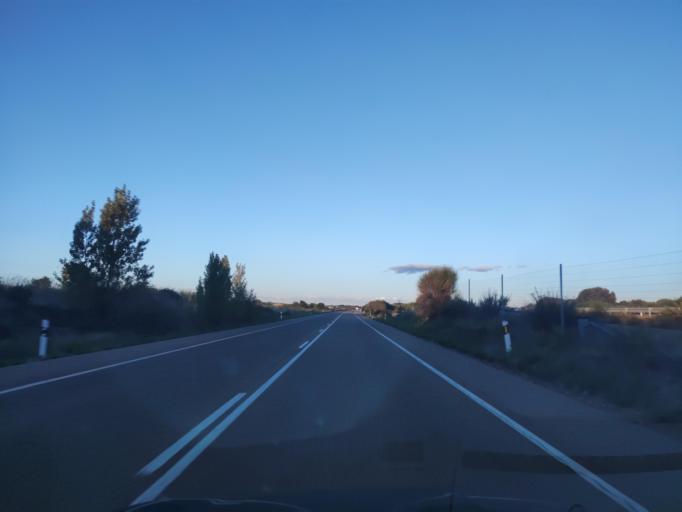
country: ES
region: Castille and Leon
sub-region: Provincia de Salamanca
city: Martin de Yeltes
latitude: 40.7654
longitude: -6.3089
